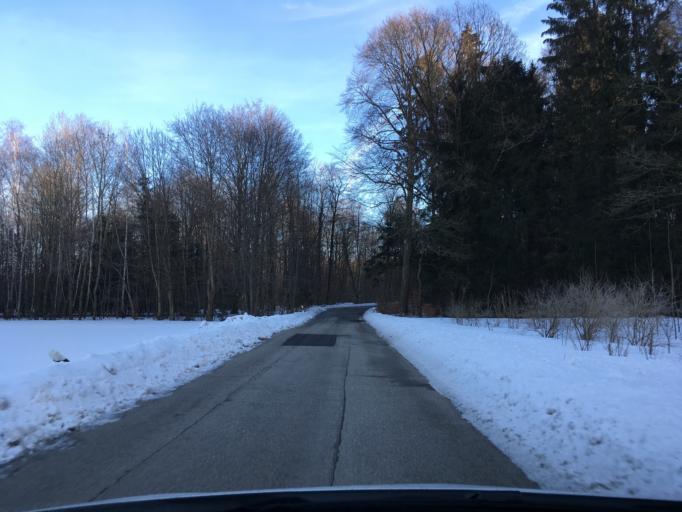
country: DE
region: Bavaria
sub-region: Upper Bavaria
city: Albaching
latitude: 48.1144
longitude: 12.0799
